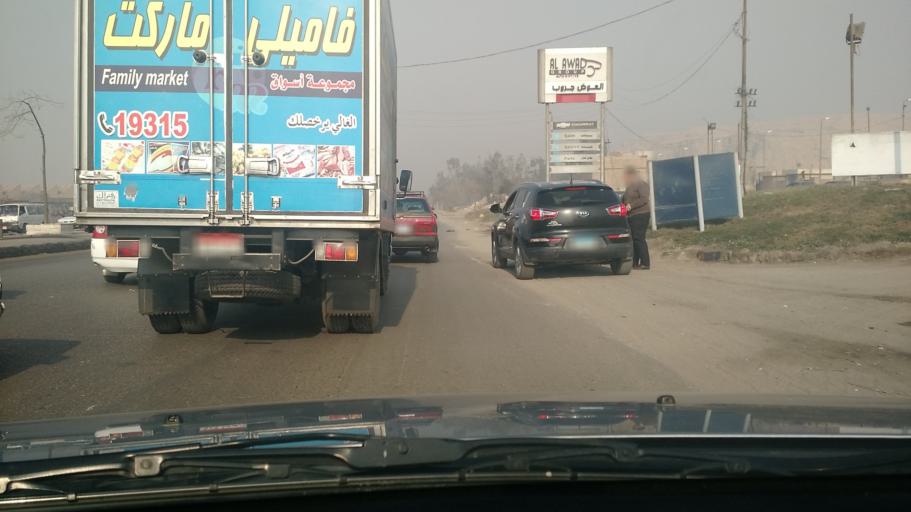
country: EG
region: Al Jizah
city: Al Jizah
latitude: 29.9956
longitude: 31.2803
